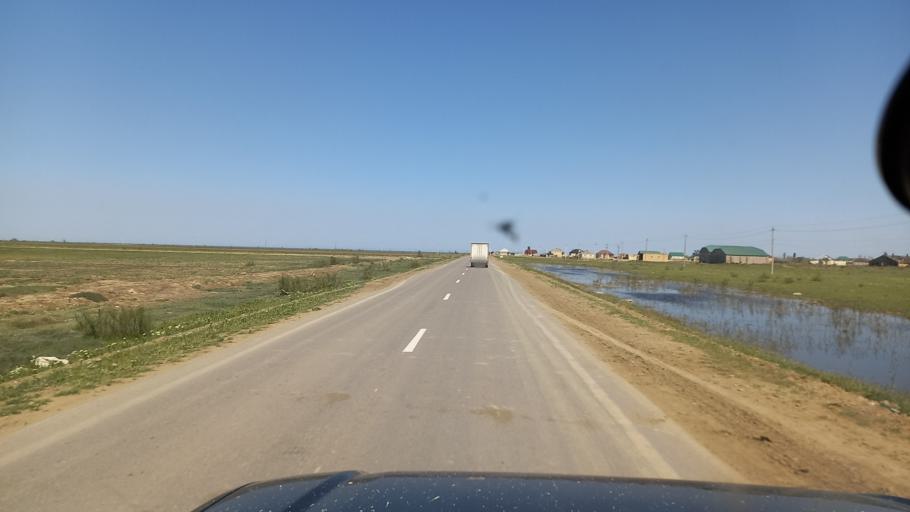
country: RU
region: Dagestan
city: Khazar
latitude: 41.9405
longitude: 48.3287
